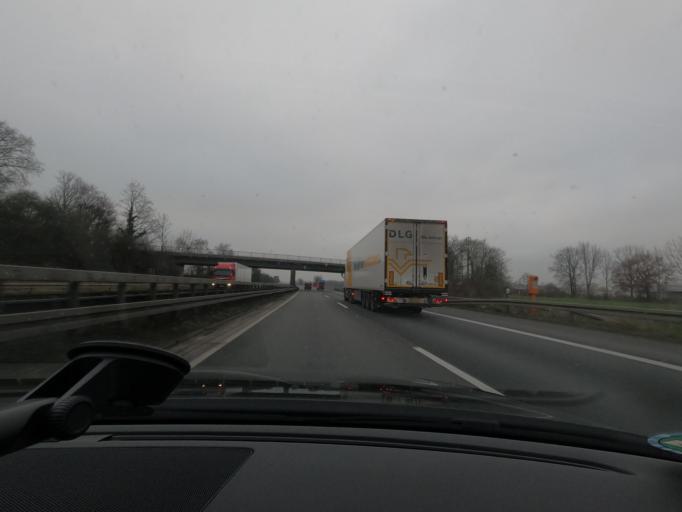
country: DE
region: North Rhine-Westphalia
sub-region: Regierungsbezirk Dusseldorf
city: Monchengladbach
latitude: 51.1486
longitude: 6.4072
